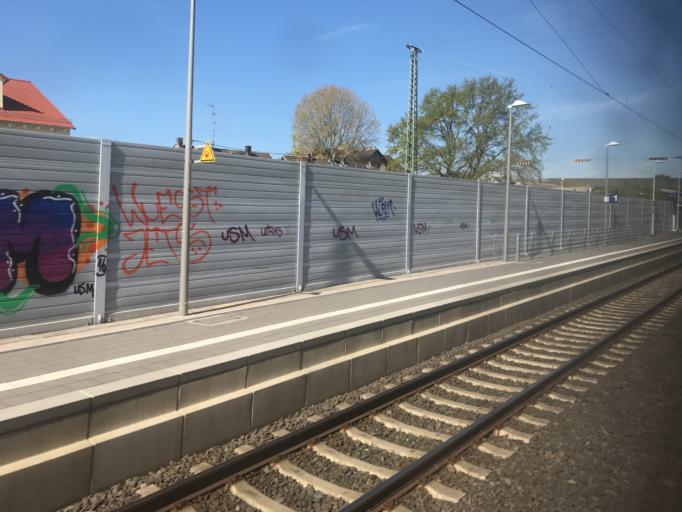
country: DE
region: Rheinland-Pfalz
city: Bodenheim
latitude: 49.9291
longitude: 8.3132
